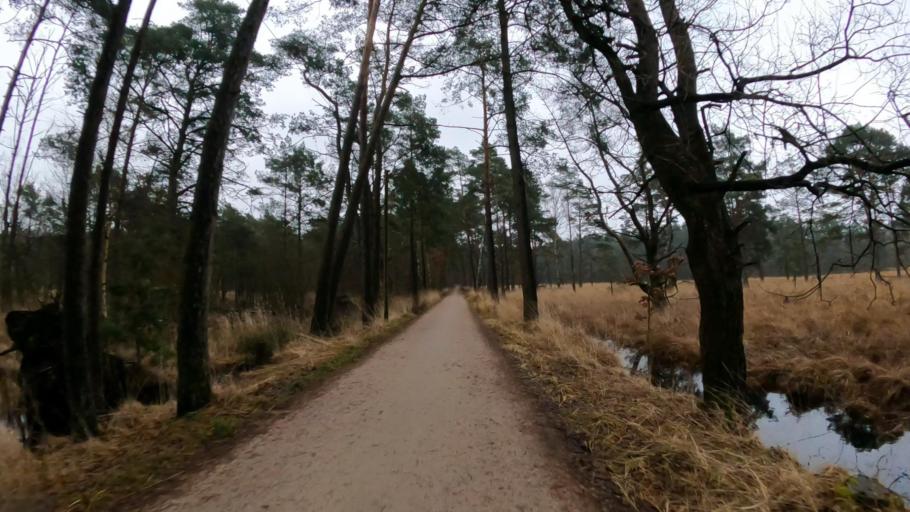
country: DE
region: Schleswig-Holstein
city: Appen
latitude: 53.6015
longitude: 9.7628
